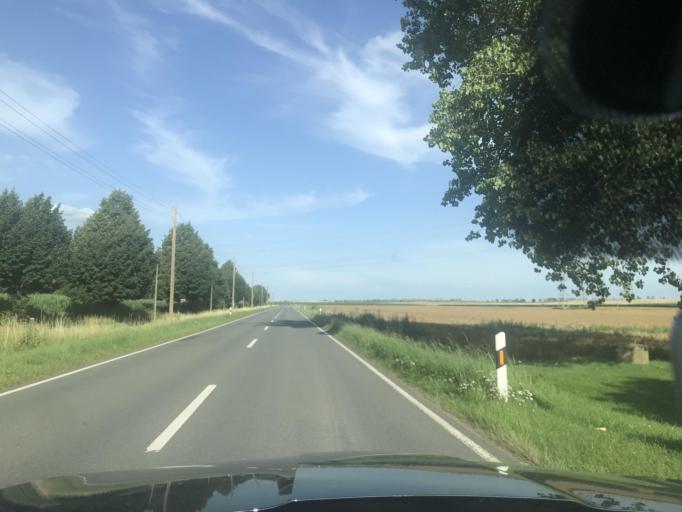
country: DE
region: Saxony-Anhalt
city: Harsleben
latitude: 51.8702
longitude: 11.1158
